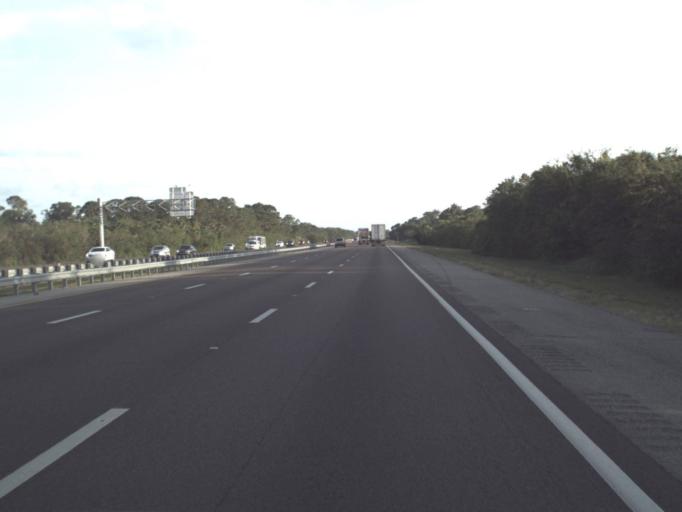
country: US
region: Florida
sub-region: Brevard County
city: Port Saint John
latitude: 28.5356
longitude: -80.8519
